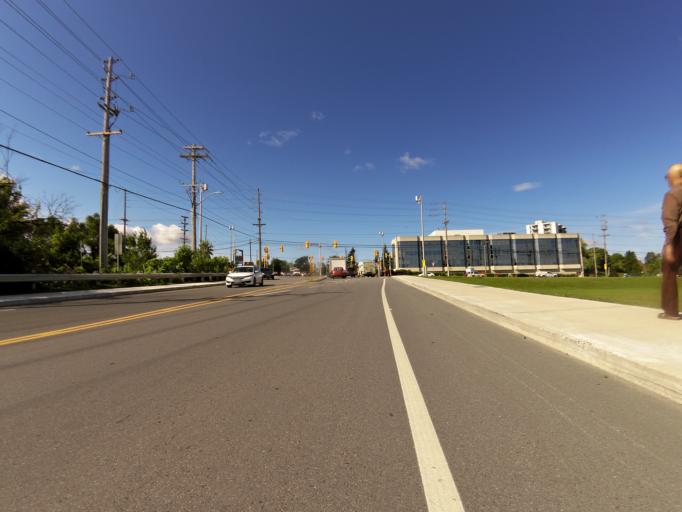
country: CA
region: Ontario
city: Ottawa
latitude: 45.4018
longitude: -75.6232
